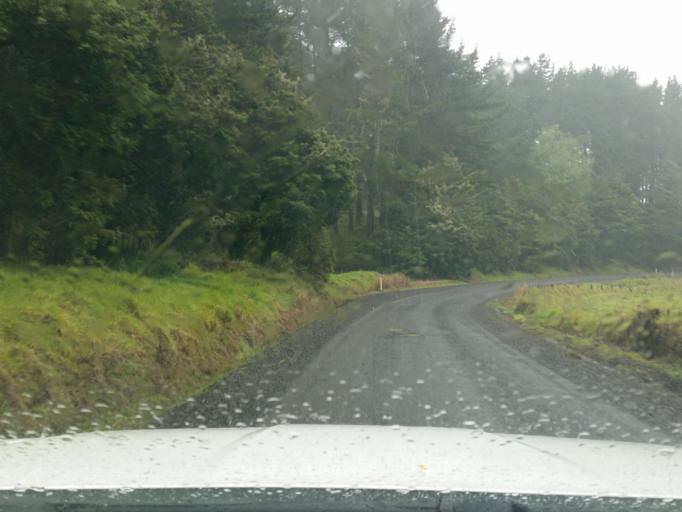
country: NZ
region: Northland
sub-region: Kaipara District
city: Dargaville
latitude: -35.8067
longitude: 173.9868
